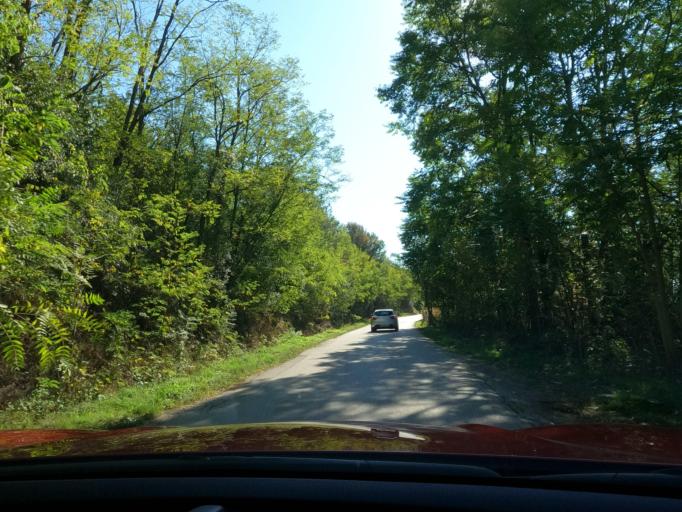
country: RS
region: Central Serbia
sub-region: Raski Okrug
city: Kraljevo
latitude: 43.7703
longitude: 20.6612
